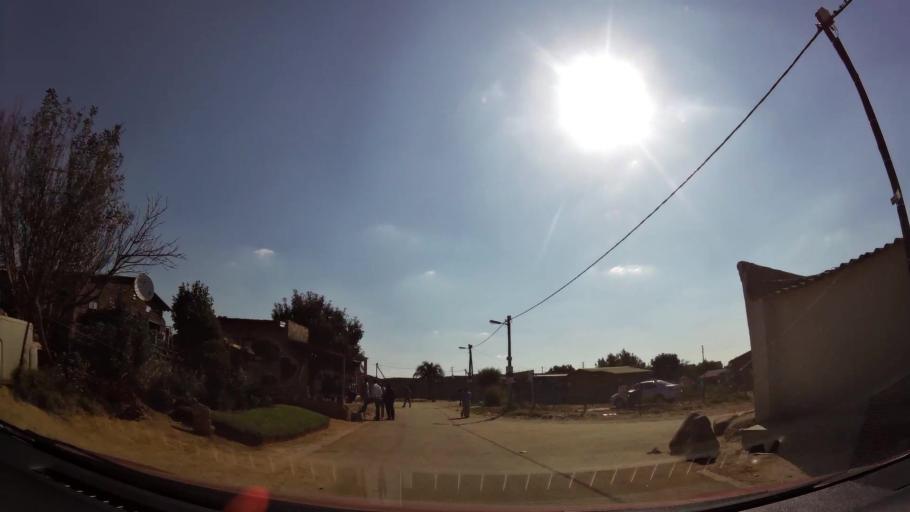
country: ZA
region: Gauteng
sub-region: West Rand District Municipality
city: Muldersdriseloop
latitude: -26.0231
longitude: 27.9268
